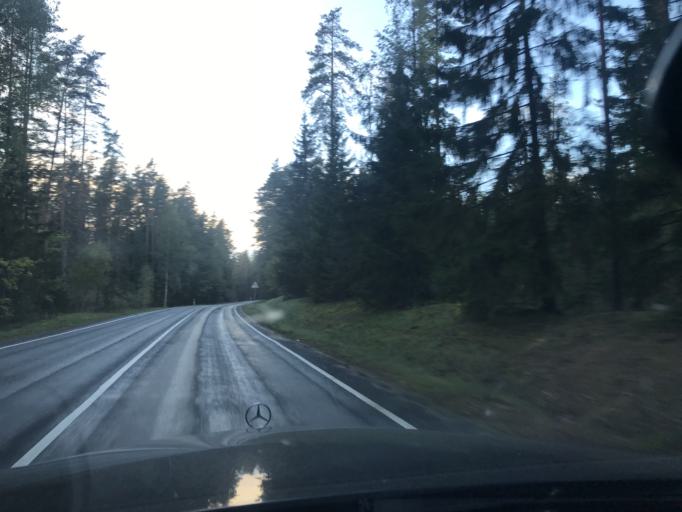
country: EE
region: Vorumaa
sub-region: Antsla vald
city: Vana-Antsla
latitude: 57.8808
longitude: 26.7551
